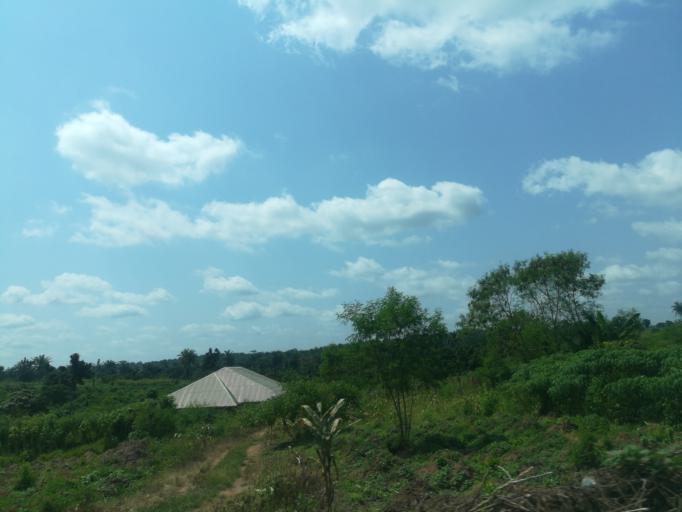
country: NG
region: Oyo
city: Moniya
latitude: 7.5725
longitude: 3.9105
